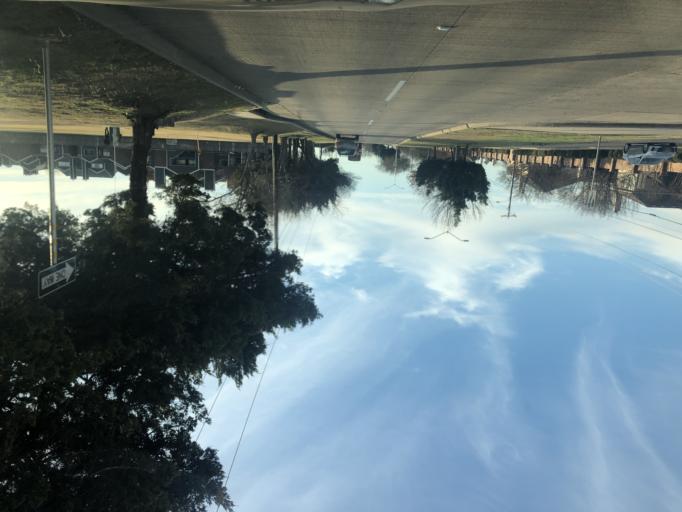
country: US
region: Texas
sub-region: Dallas County
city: Cedar Hill
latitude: 32.5951
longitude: -96.9255
